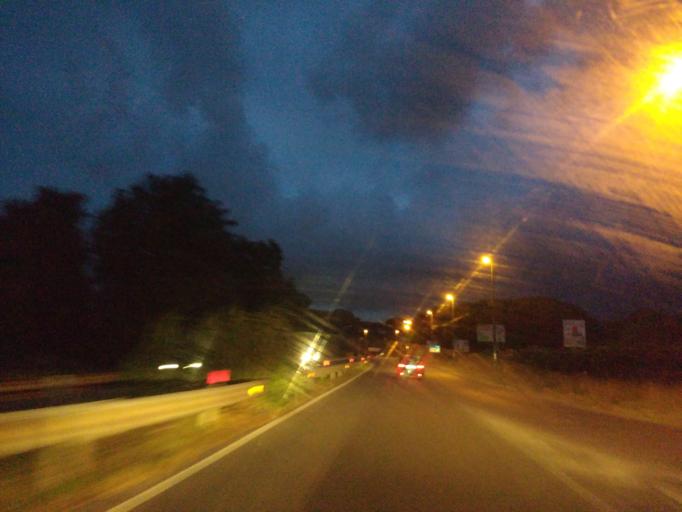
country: IT
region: Latium
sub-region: Citta metropolitana di Roma Capitale
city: Anzio
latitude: 41.4623
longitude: 12.6217
